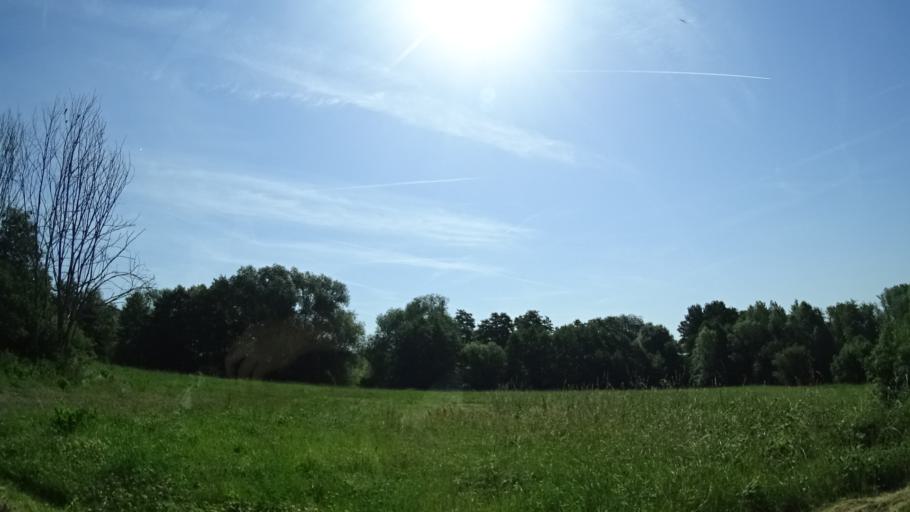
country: DE
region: Hesse
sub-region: Regierungsbezirk Giessen
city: Rabenau
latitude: 50.6905
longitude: 8.8257
